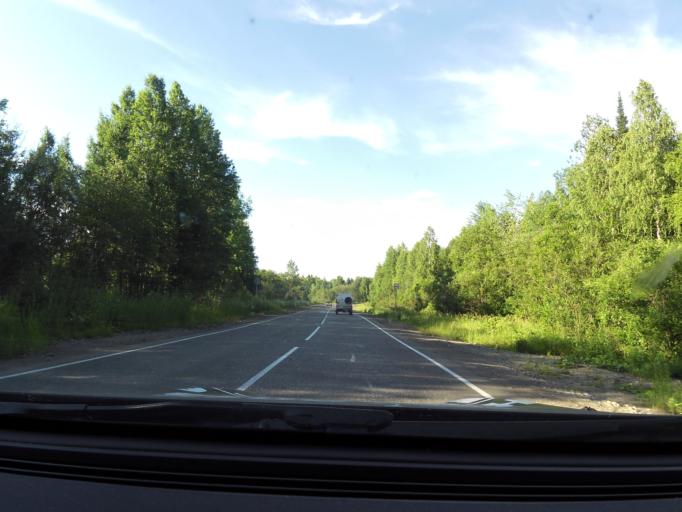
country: RU
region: Kirov
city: Belorechensk
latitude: 58.7627
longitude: 52.3595
